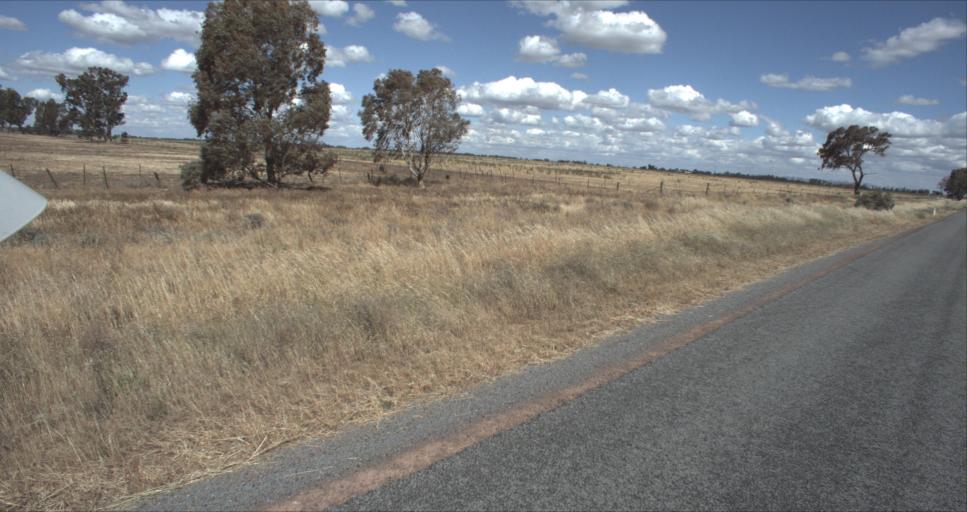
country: AU
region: New South Wales
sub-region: Leeton
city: Leeton
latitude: -34.4920
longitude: 146.2471
